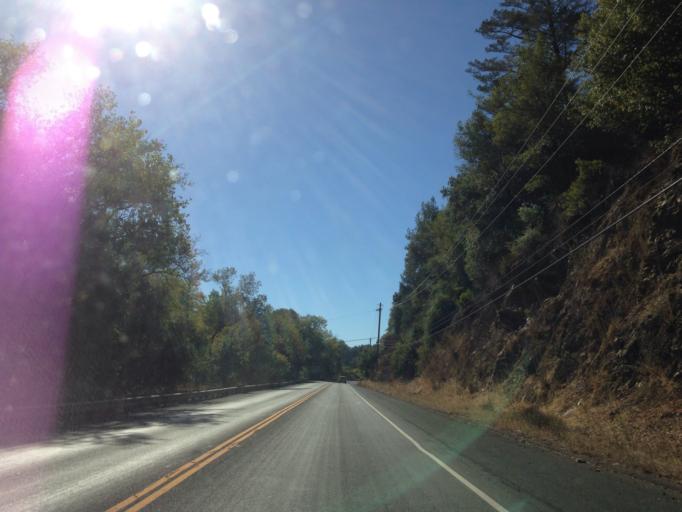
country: US
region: California
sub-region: Sonoma County
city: Guerneville
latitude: 38.5068
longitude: -122.9483
